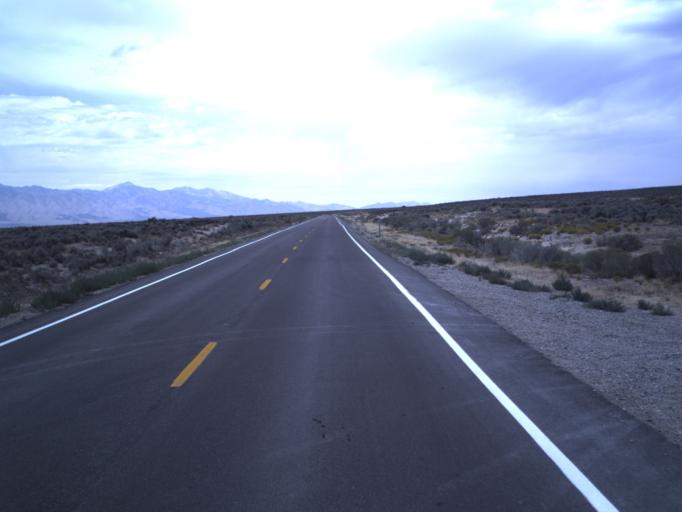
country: US
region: Utah
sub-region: Tooele County
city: Tooele
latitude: 40.2849
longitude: -112.2632
